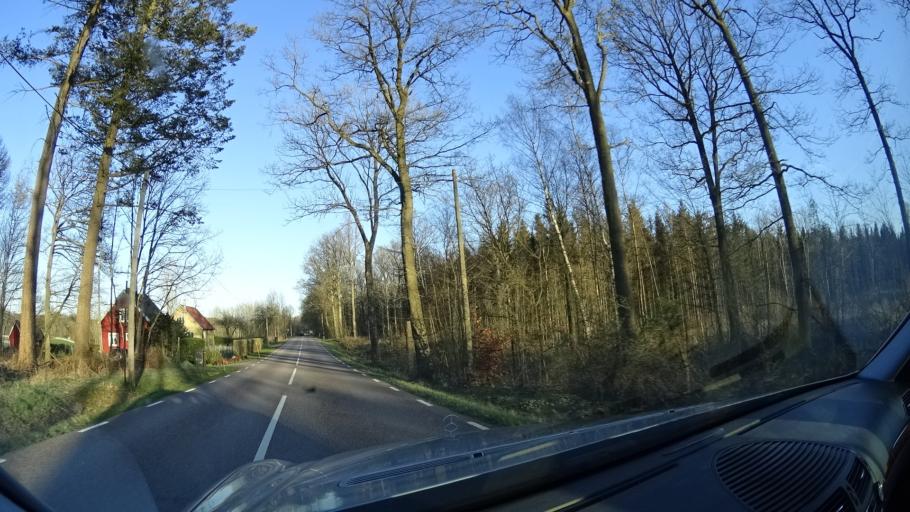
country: SE
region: Skane
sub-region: Svalovs Kommun
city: Kagerod
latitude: 55.9851
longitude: 13.1156
